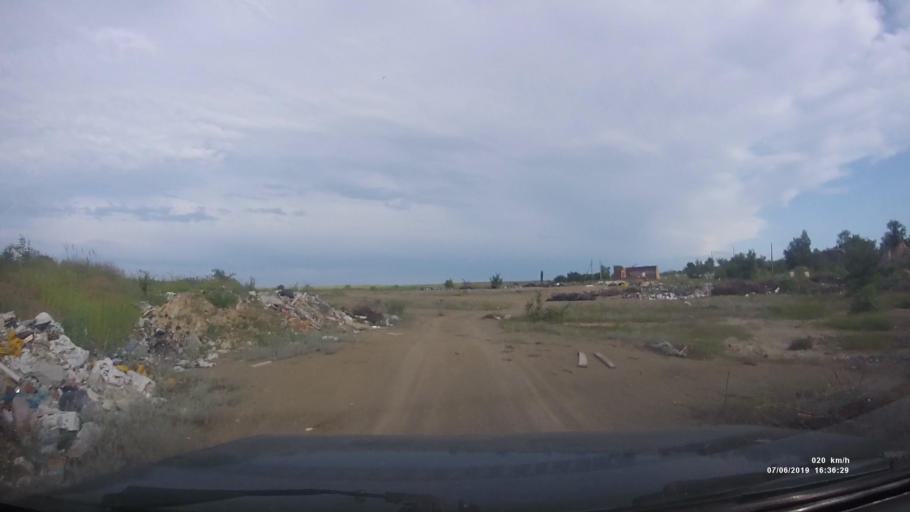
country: RU
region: Rostov
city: Staraya Stanitsa
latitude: 48.2531
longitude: 40.3520
